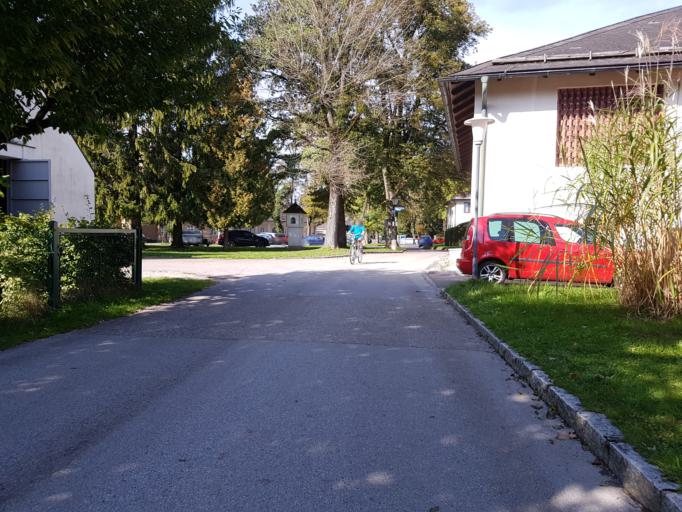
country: AT
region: Salzburg
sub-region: Salzburg Stadt
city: Salzburg
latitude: 47.7774
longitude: 13.0498
